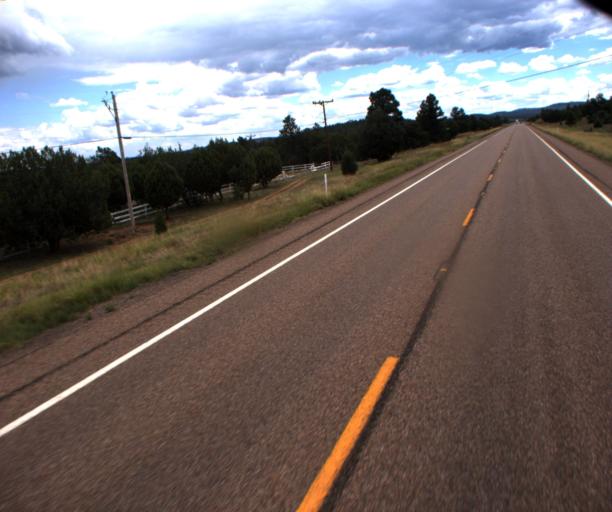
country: US
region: Arizona
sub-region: Navajo County
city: Linden
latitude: 34.3272
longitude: -110.2602
